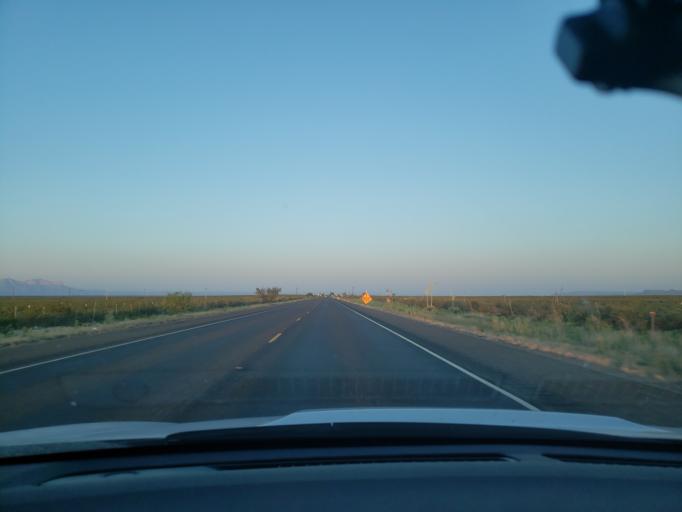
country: US
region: Texas
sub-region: Hudspeth County
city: Sierra Blanca
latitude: 31.7633
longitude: -105.3785
